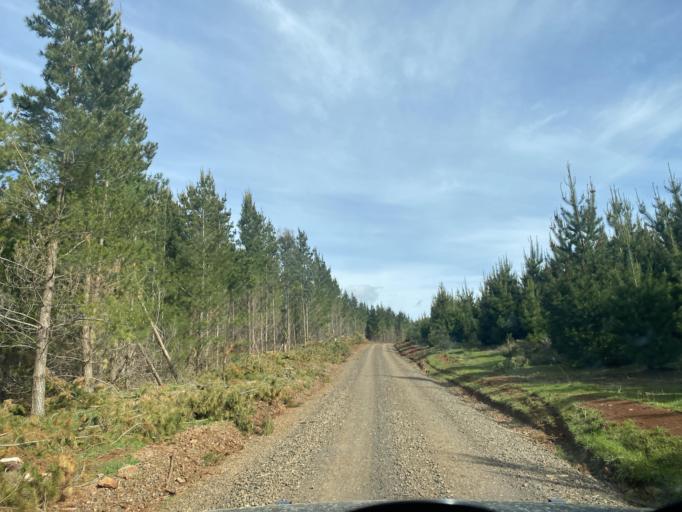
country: AU
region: Victoria
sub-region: Mansfield
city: Mansfield
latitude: -36.8314
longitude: 146.1793
